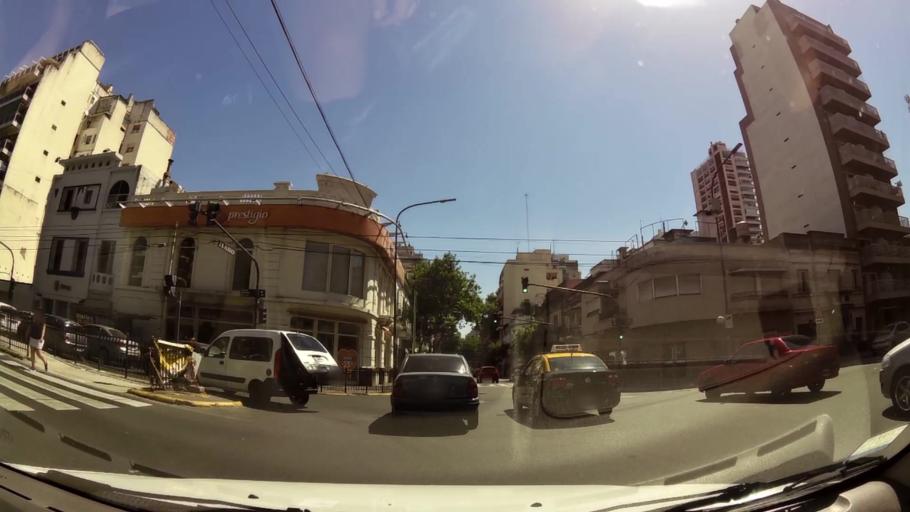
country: AR
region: Buenos Aires F.D.
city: Villa Santa Rita
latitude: -34.6293
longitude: -58.4554
